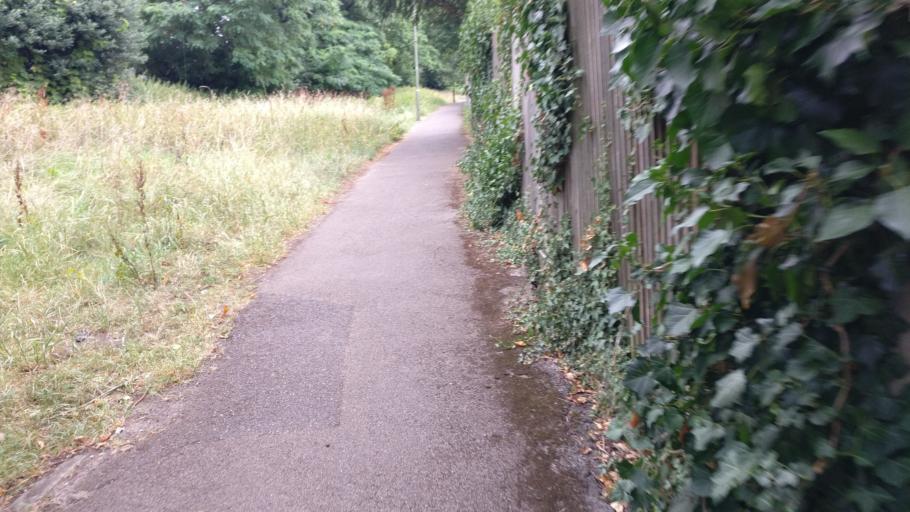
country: GB
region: England
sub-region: Surrey
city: Weybridge
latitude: 51.3722
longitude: -0.4456
